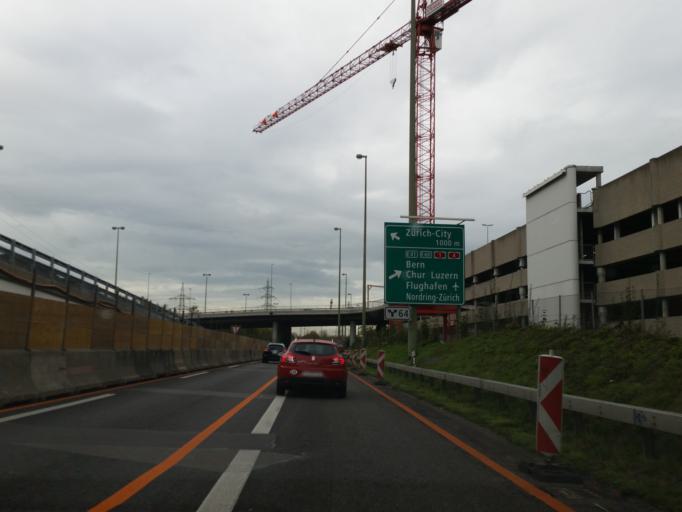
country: CH
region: Zurich
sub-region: Bezirk Buelach
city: Wallisellen / Wallisellen-Ost
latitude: 47.4077
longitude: 8.5946
